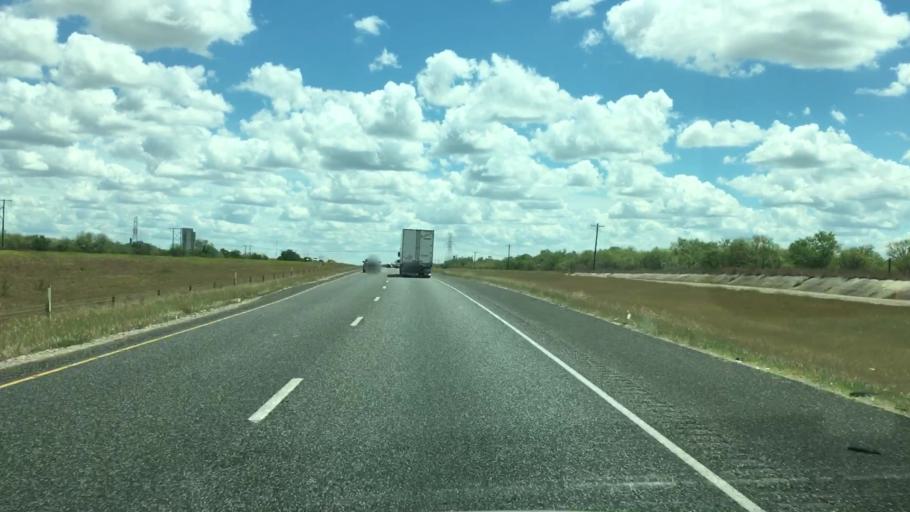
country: US
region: Texas
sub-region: Atascosa County
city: Pleasanton
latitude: 28.8286
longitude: -98.3679
